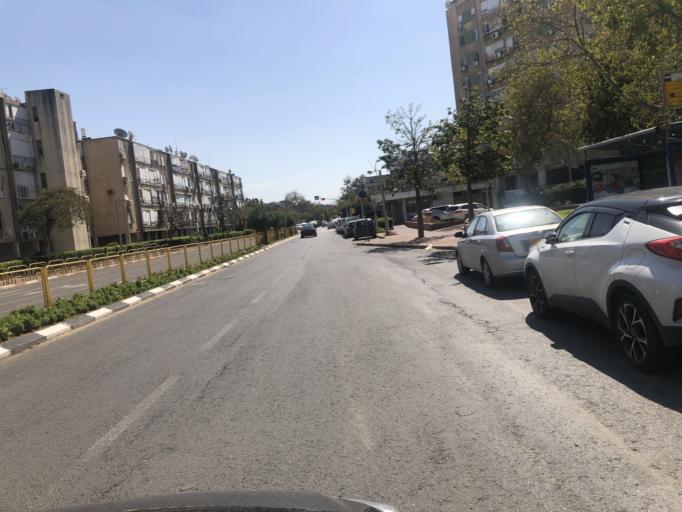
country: IL
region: Tel Aviv
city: Holon
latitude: 32.0142
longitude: 34.7648
